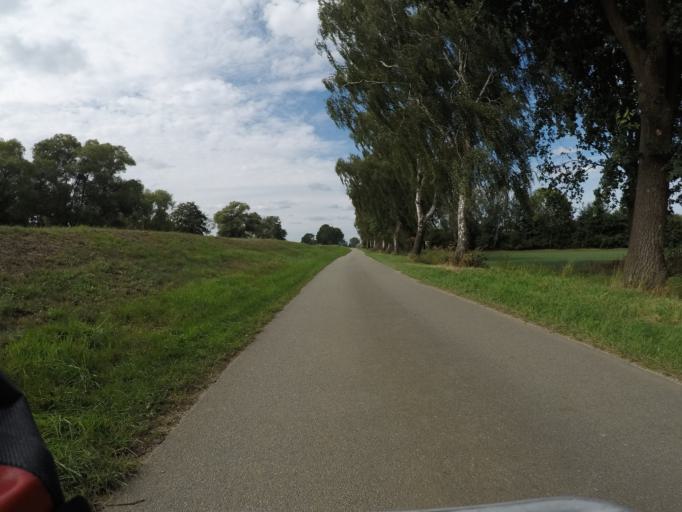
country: DE
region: Lower Saxony
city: Wittorf
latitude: 53.3453
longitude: 10.3846
